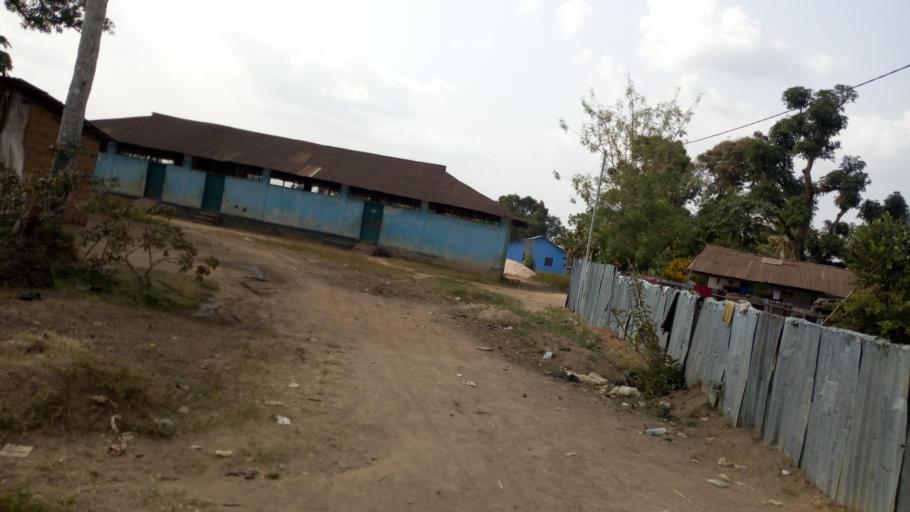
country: SL
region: Southern Province
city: Mogbwemo
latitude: 7.7645
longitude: -12.3093
